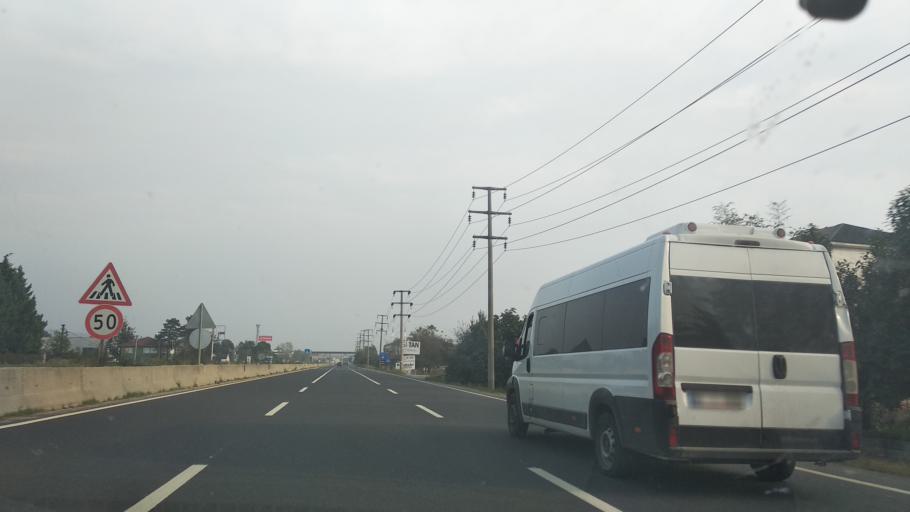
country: TR
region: Duzce
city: Duzce
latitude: 40.8082
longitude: 31.2279
